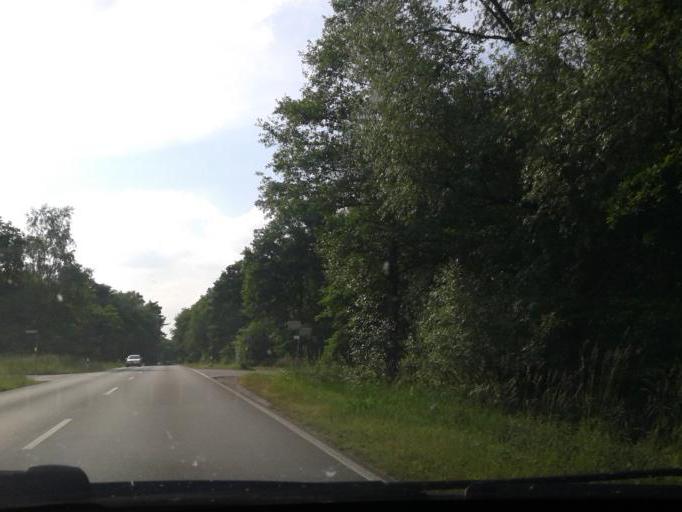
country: DE
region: North Rhine-Westphalia
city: Bad Lippspringe
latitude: 51.7727
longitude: 8.7939
